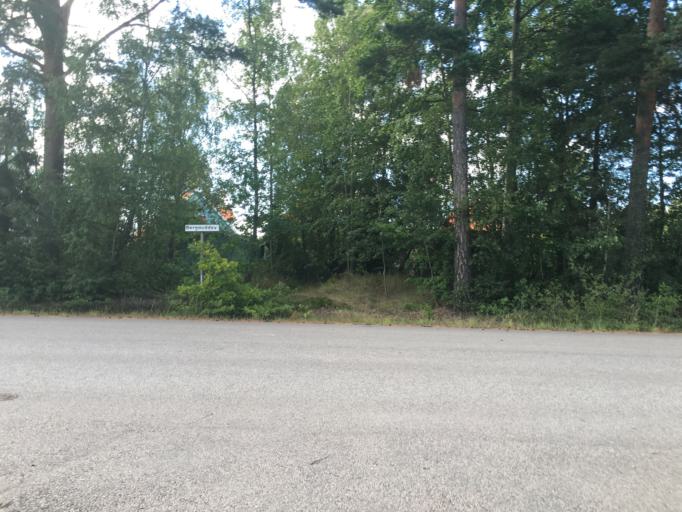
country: SE
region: Kalmar
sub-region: Kalmar Kommun
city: Kalmar
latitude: 56.6999
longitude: 16.3647
